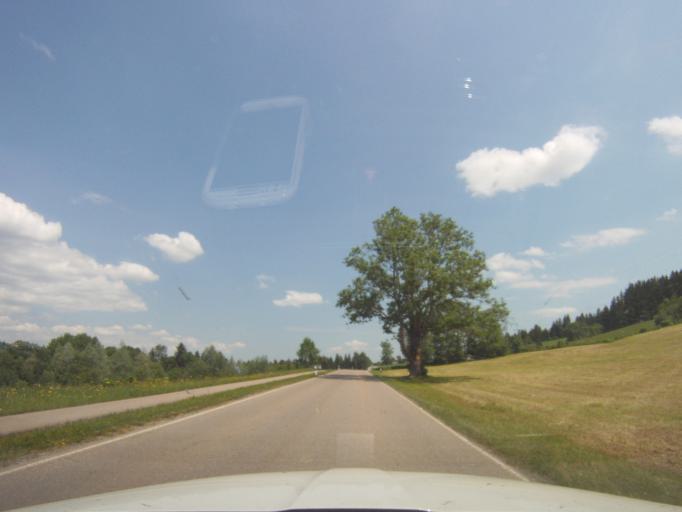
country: DE
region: Bavaria
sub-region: Swabia
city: Oy-Mittelberg
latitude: 47.6067
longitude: 10.4426
